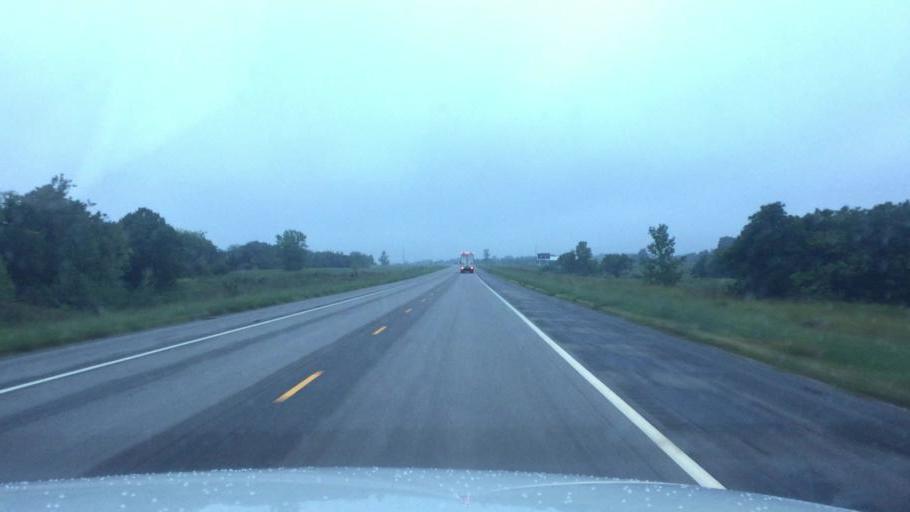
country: US
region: Kansas
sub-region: Montgomery County
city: Cherryvale
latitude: 37.4622
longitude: -95.4797
